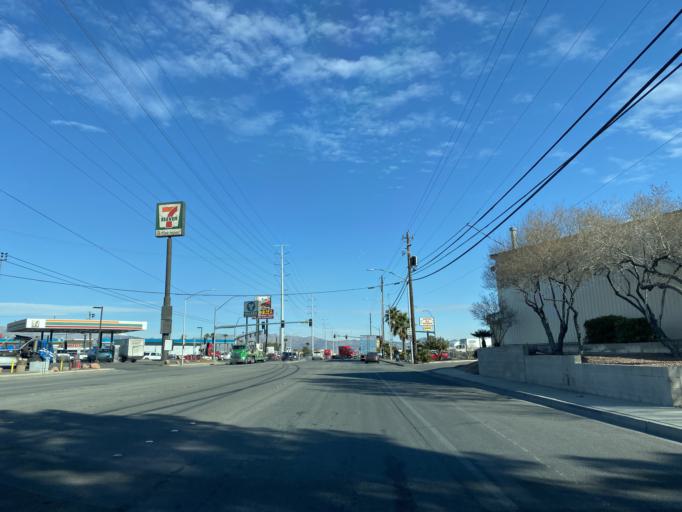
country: US
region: Nevada
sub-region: Clark County
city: North Las Vegas
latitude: 36.2166
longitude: -115.1279
